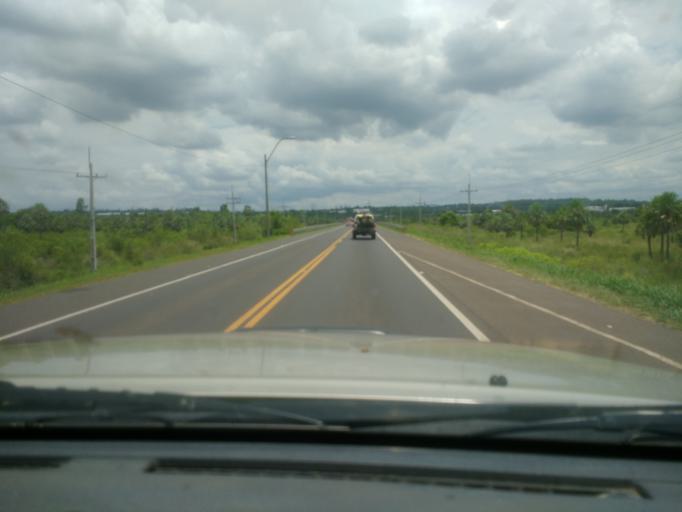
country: PY
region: Central
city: Limpio
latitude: -25.1253
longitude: -57.4393
